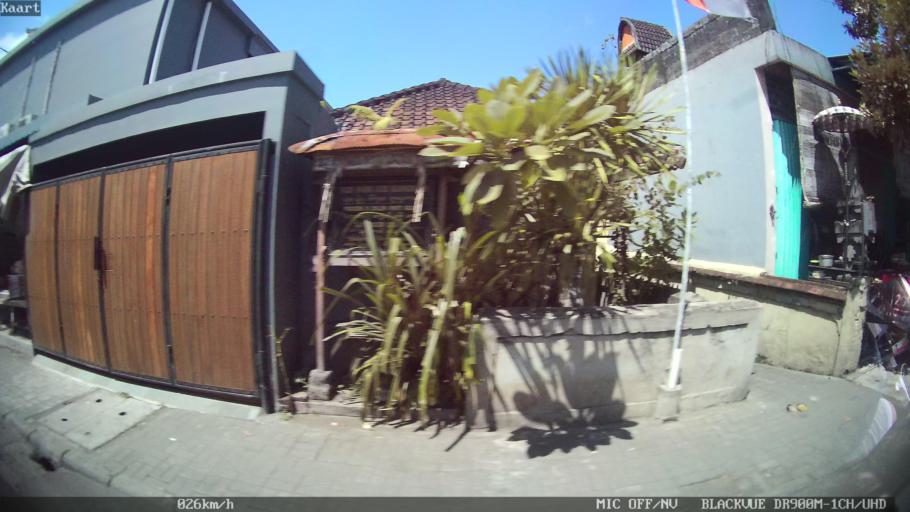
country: ID
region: Bali
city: Banjar Gunungpande
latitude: -8.6531
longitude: 115.1625
